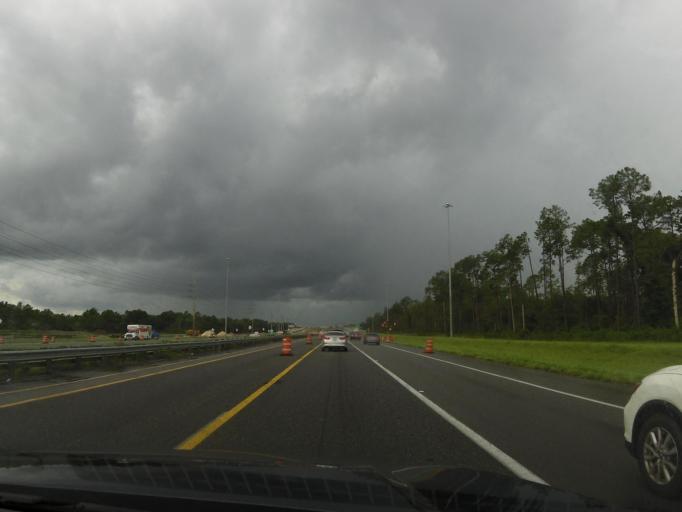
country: US
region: Florida
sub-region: Duval County
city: Baldwin
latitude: 30.2911
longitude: -81.9696
